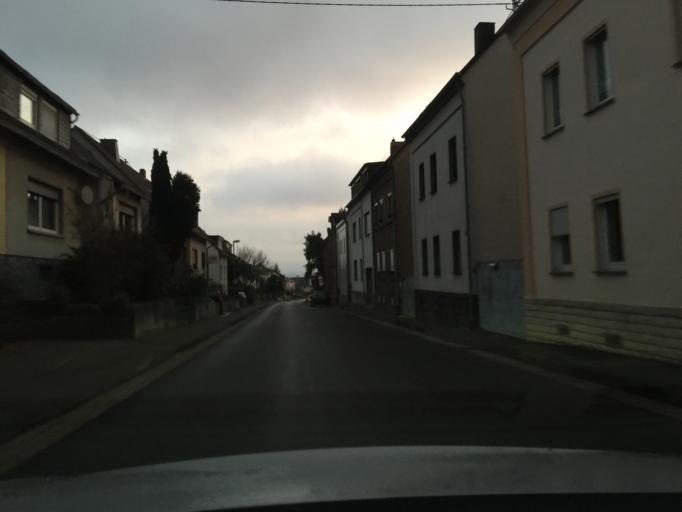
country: DE
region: Rheinland-Pfalz
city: Mulheim-Karlich
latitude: 50.3737
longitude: 7.5261
